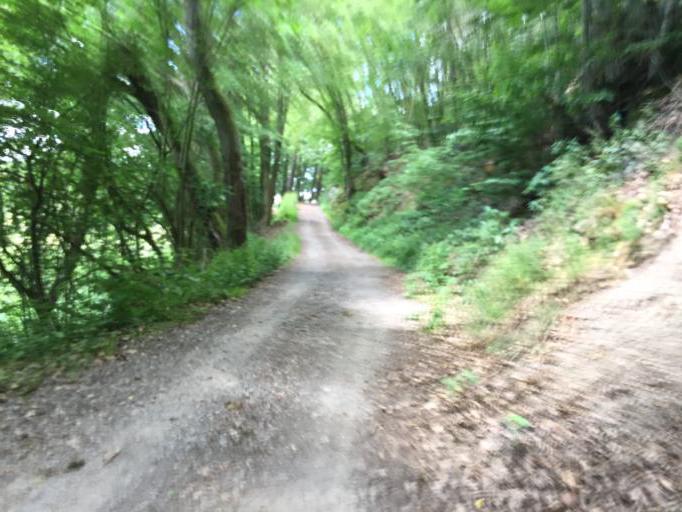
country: DE
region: Rheinland-Pfalz
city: Holler
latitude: 50.4256
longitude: 7.8520
